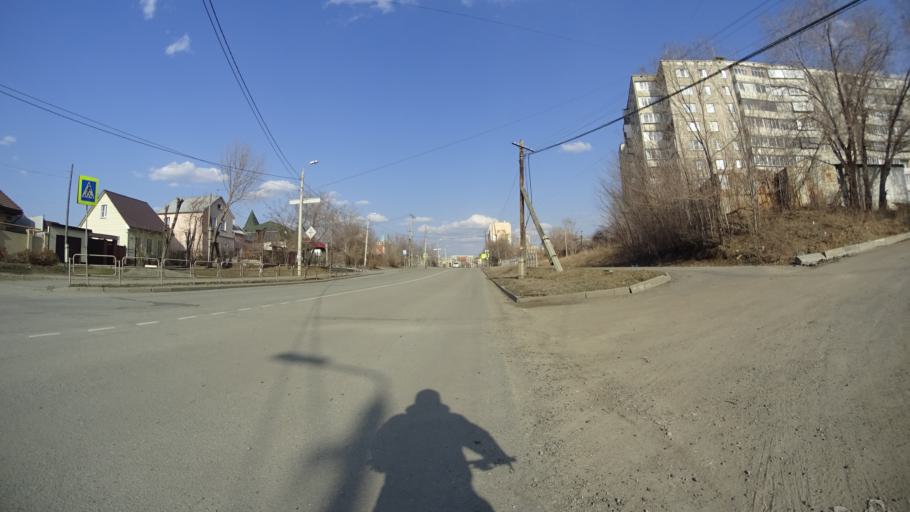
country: RU
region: Chelyabinsk
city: Novosineglazovskiy
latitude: 55.1123
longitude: 61.3356
